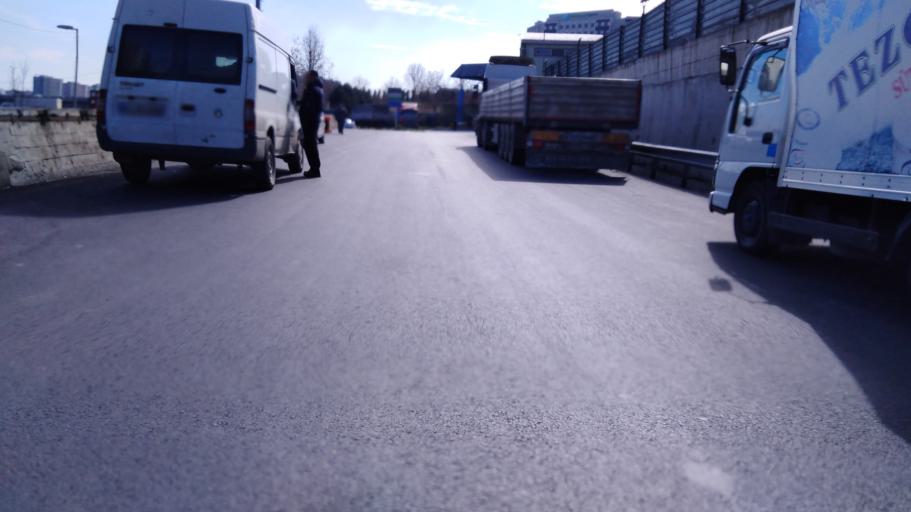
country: TR
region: Istanbul
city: Esenler
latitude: 41.0469
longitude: 28.8909
